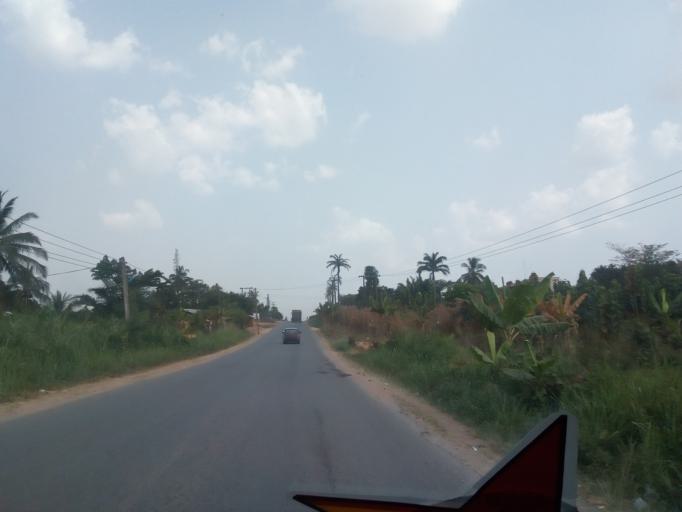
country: GH
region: Eastern
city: Suhum
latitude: 6.0416
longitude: -0.4416
